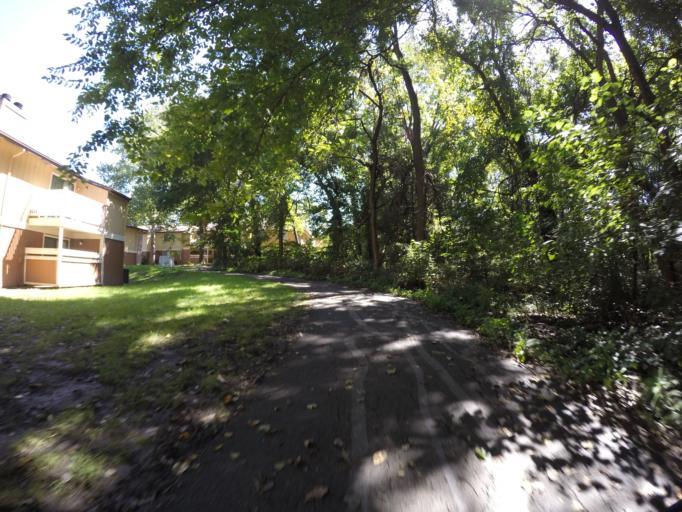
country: US
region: Kansas
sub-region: Johnson County
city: Overland Park
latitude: 38.9349
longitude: -94.6772
